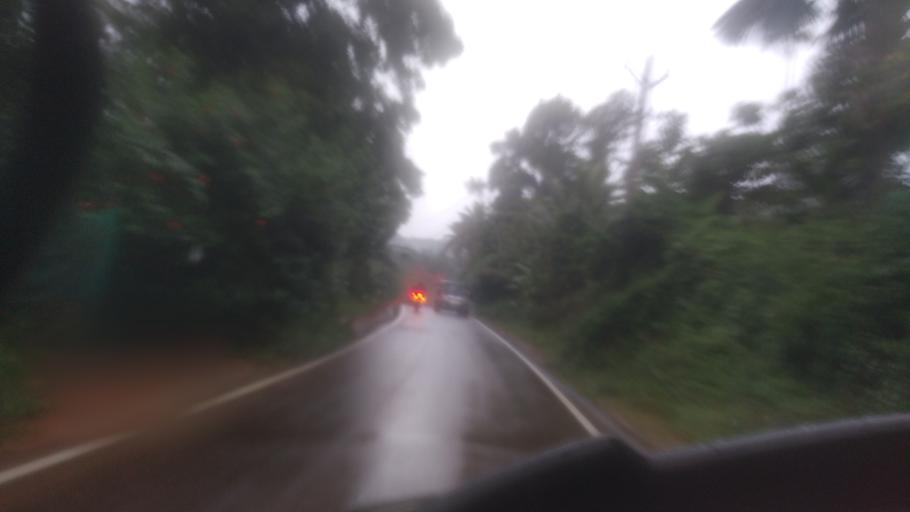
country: IN
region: Kerala
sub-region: Idukki
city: Idukki
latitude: 9.9305
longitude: 77.0699
